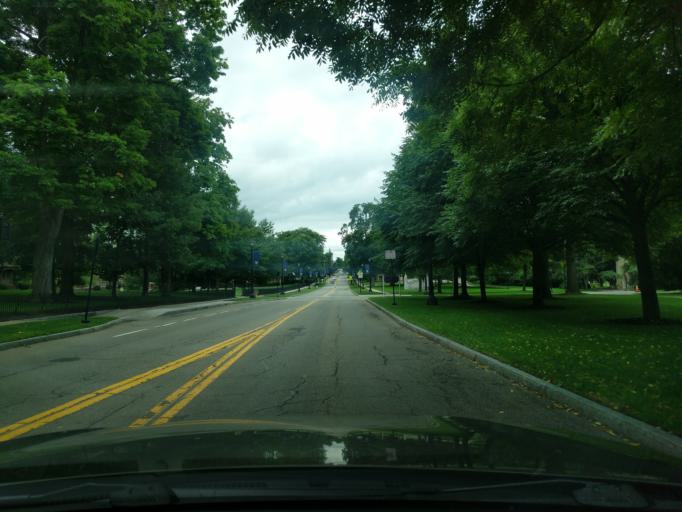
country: US
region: New York
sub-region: Chemung County
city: Elmira
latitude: 42.0983
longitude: -76.8149
